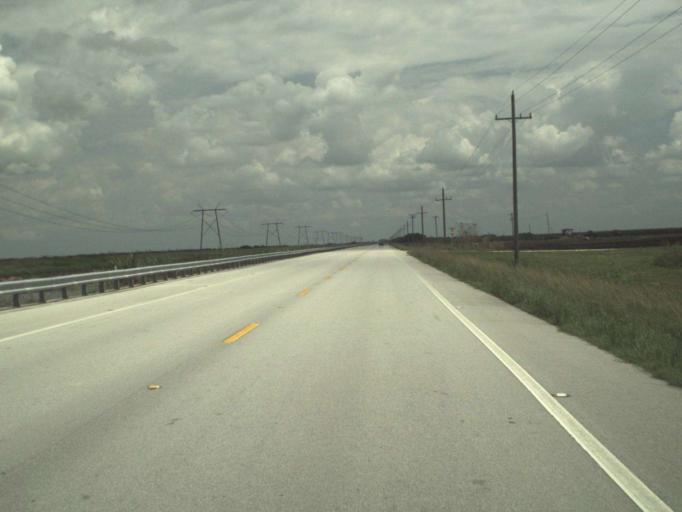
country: US
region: Florida
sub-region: Palm Beach County
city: Loxahatchee Groves
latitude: 26.7406
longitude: -80.4679
